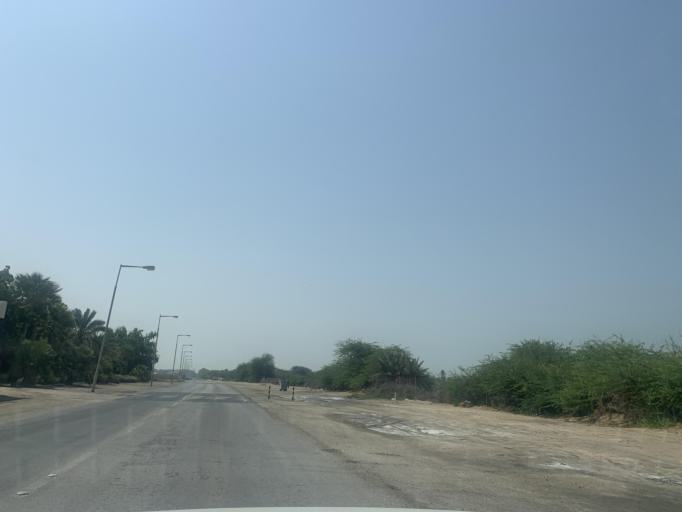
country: BH
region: Central Governorate
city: Madinat Hamad
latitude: 26.1663
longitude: 50.4567
